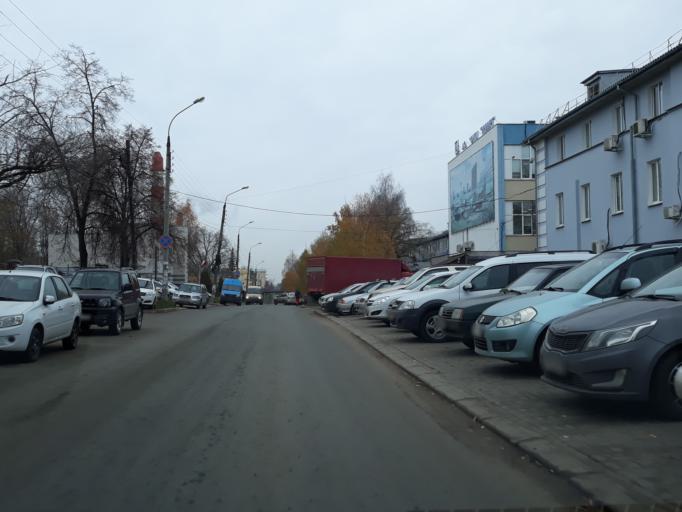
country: RU
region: Nizjnij Novgorod
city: Nizhniy Novgorod
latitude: 56.2499
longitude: 43.9785
